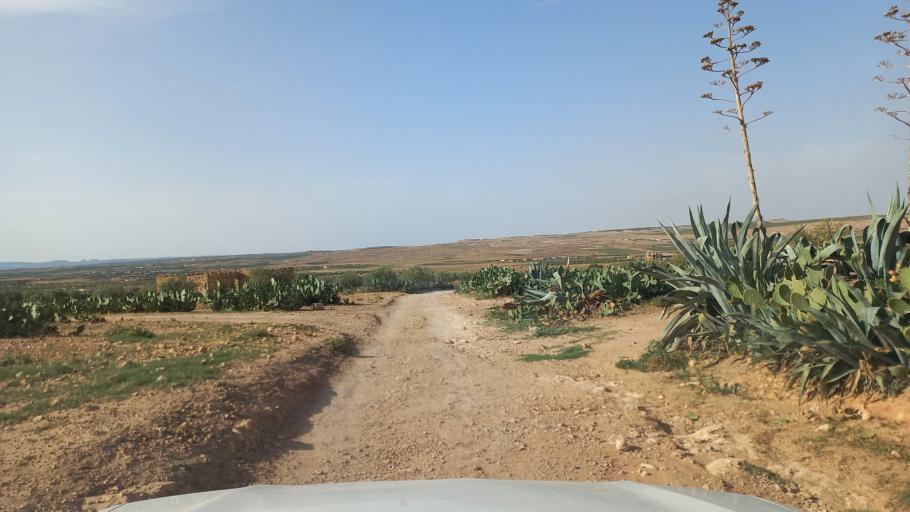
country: TN
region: Al Qasrayn
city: Kasserine
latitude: 35.3359
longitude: 8.8452
